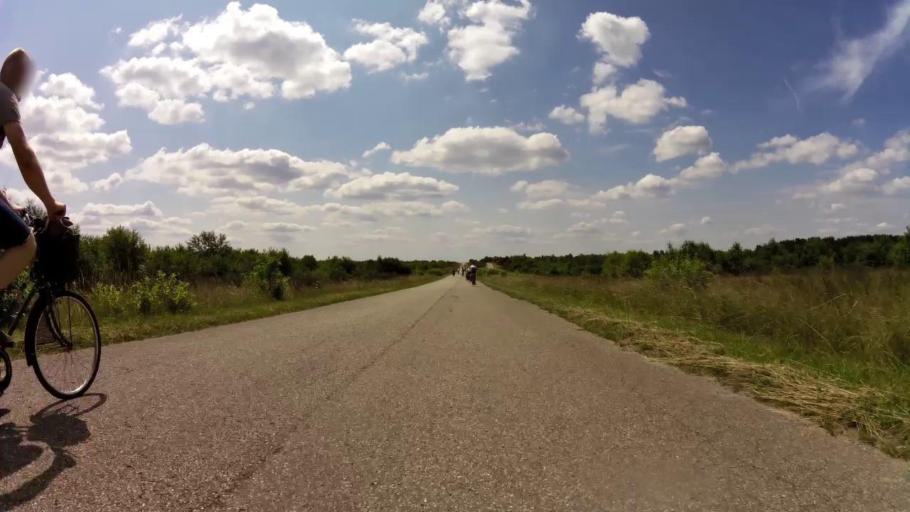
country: PL
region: West Pomeranian Voivodeship
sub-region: Powiat drawski
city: Drawsko Pomorskie
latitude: 53.4374
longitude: 15.7564
